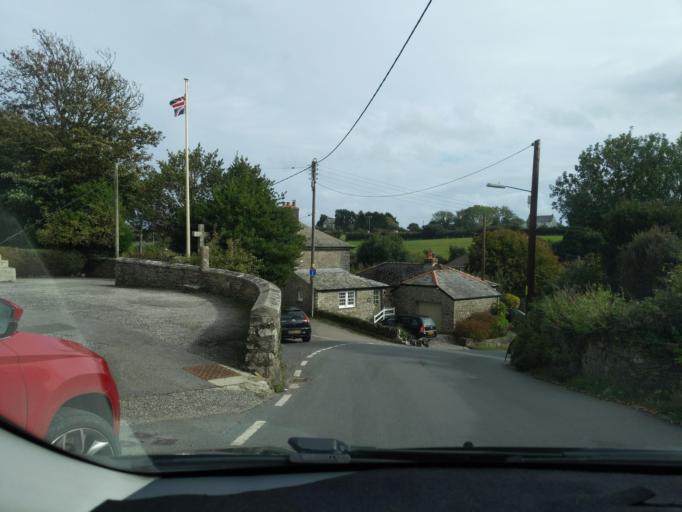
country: GB
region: England
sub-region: Cornwall
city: Mevagissey
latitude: 50.2465
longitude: -4.8080
